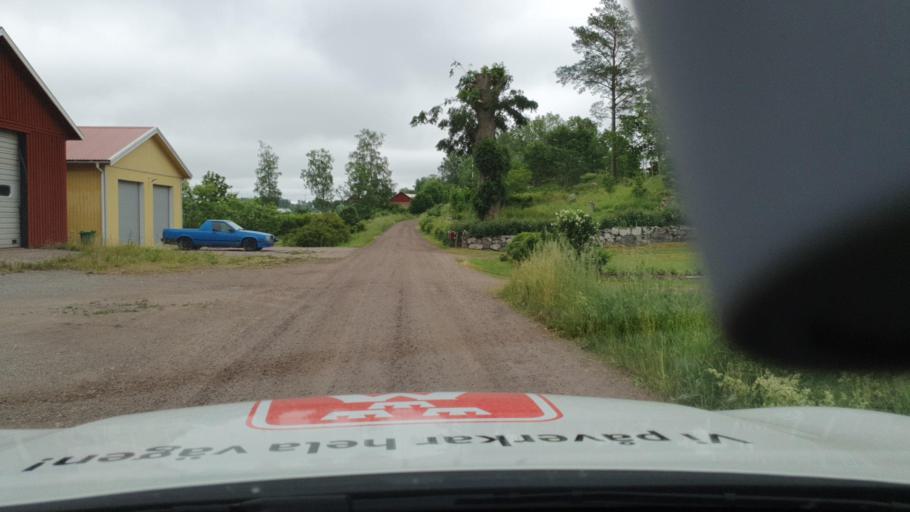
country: SE
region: Vaestra Goetaland
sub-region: Skovde Kommun
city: Stopen
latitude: 58.4004
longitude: 13.9894
